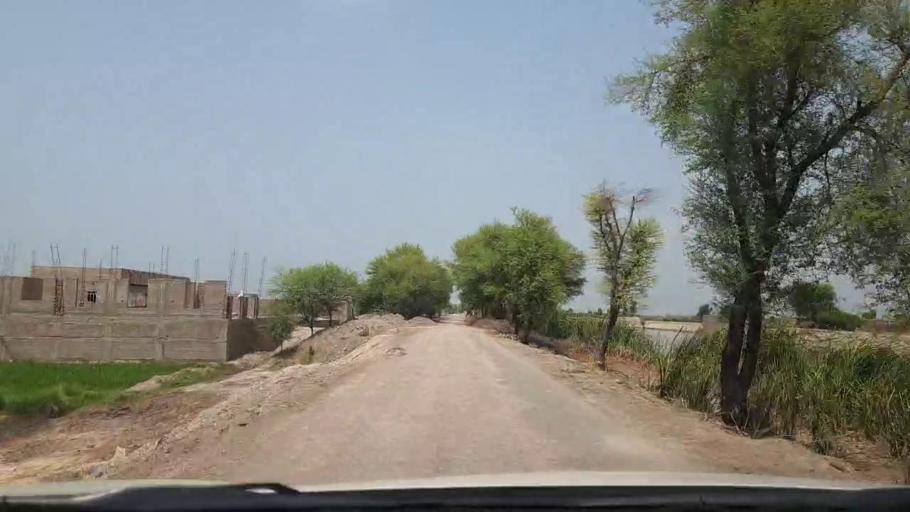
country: PK
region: Sindh
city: Dokri
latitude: 27.3367
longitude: 68.1103
